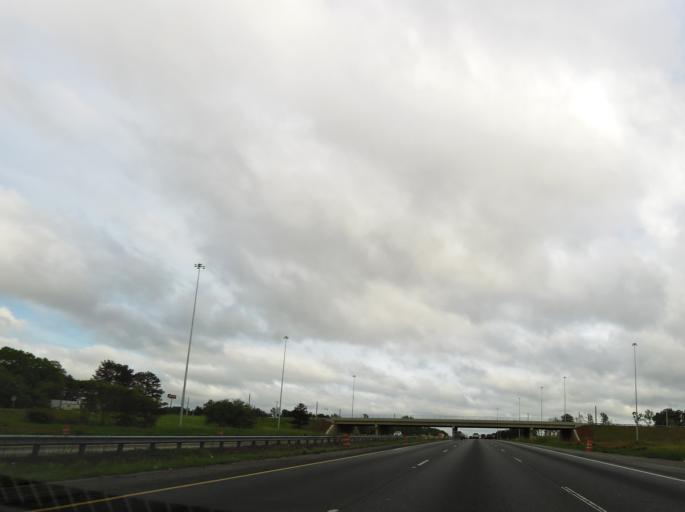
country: US
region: Georgia
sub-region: Henry County
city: Stockbridge
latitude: 33.4846
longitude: -84.2181
